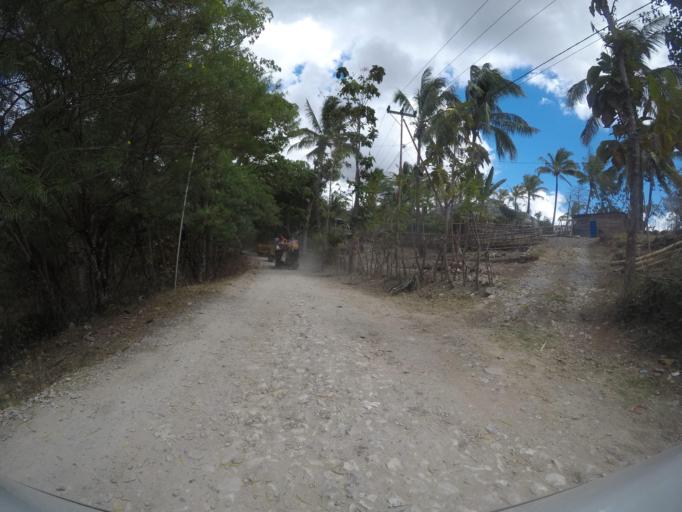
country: TL
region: Baucau
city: Baucau
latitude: -8.5046
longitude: 126.6793
